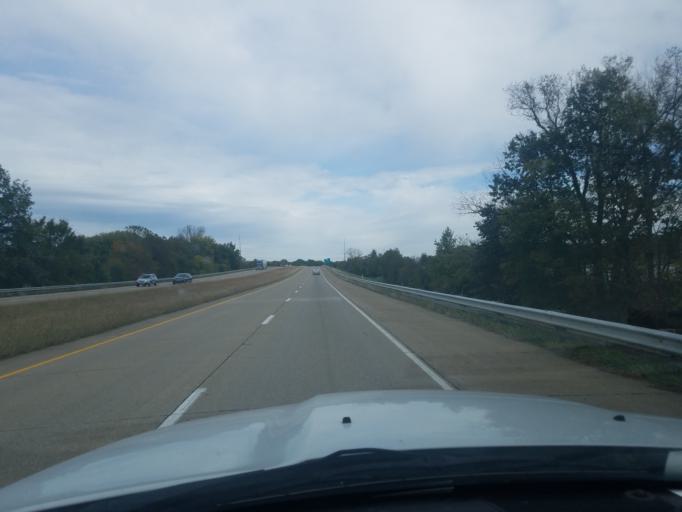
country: US
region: Indiana
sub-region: Warrick County
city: Newburgh
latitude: 37.9453
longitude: -87.4755
